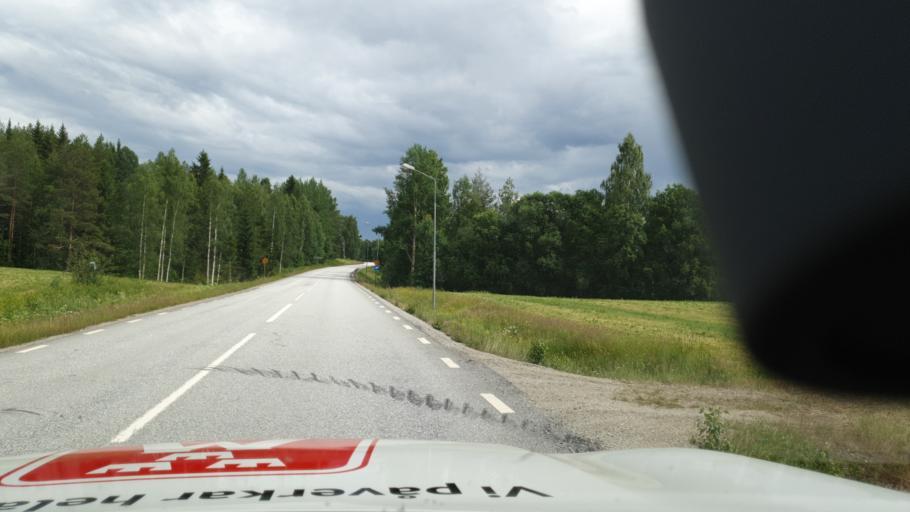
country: SE
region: Vaesterbotten
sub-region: Vindelns Kommun
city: Vindeln
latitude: 64.1299
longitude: 19.5399
